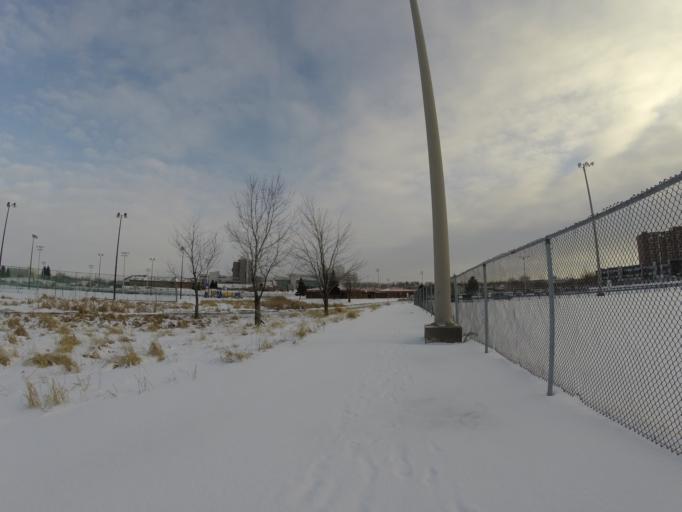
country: CA
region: Ontario
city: Greater Sudbury
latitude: 46.4698
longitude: -81.0012
